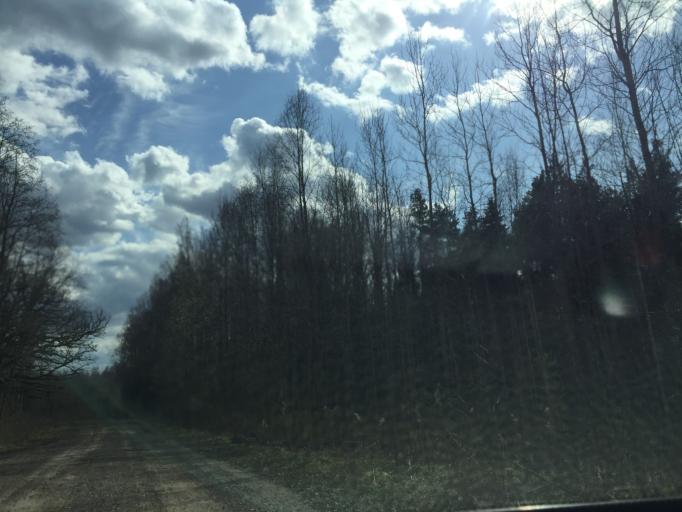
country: LV
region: Skriveri
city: Skriveri
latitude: 56.7985
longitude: 25.1333
